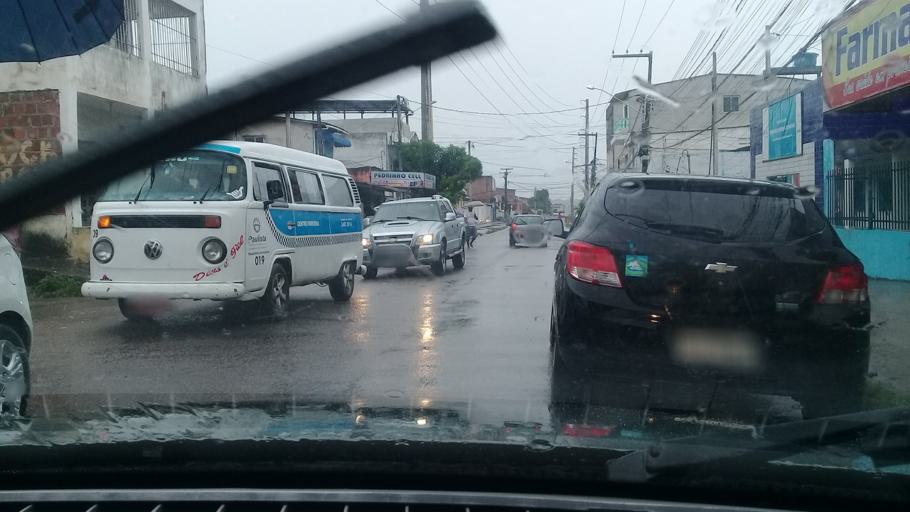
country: BR
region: Pernambuco
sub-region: Paulista
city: Paulista
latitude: -7.9596
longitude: -34.8907
